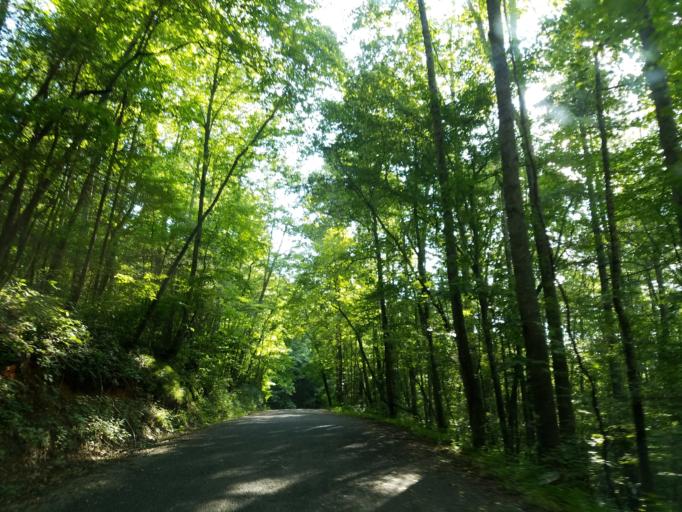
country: US
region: Georgia
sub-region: Gilmer County
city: Ellijay
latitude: 34.6308
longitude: -84.2589
